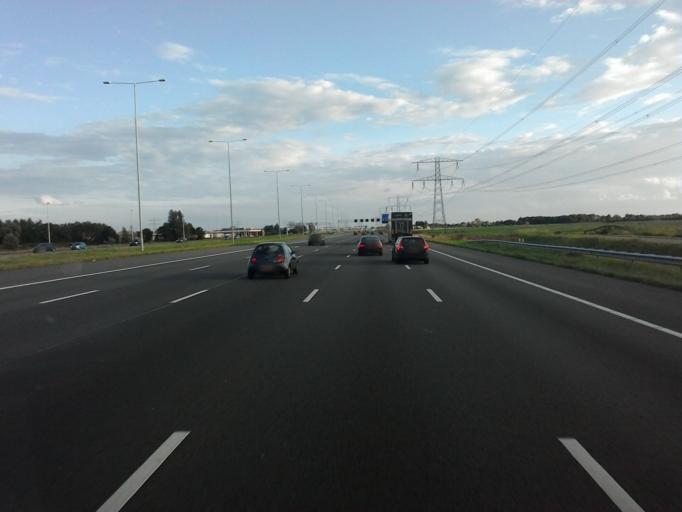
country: NL
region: Utrecht
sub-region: Stichtse Vecht
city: Breukelen
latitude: 52.1885
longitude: 4.9861
